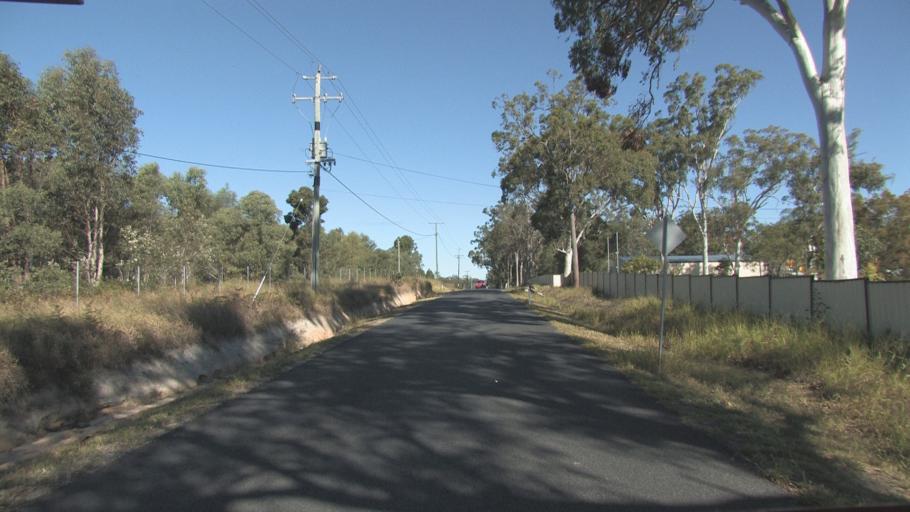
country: AU
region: Queensland
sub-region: Logan
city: Logan Reserve
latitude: -27.7212
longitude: 153.0739
